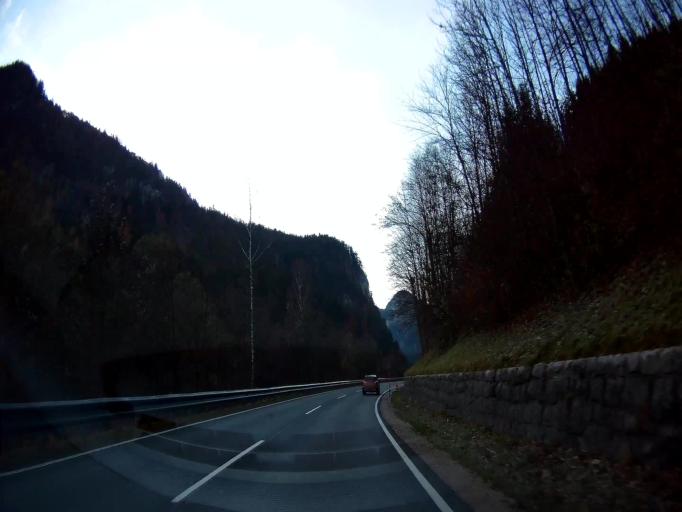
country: AT
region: Salzburg
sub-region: Politischer Bezirk Zell am See
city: Unken
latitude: 47.6429
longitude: 12.7233
